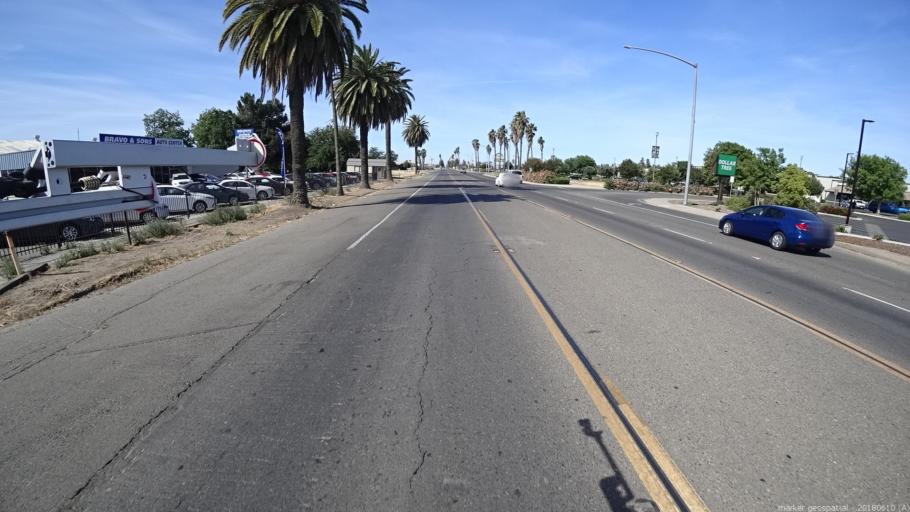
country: US
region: California
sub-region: Madera County
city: Chowchilla
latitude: 37.1117
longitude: -120.2733
